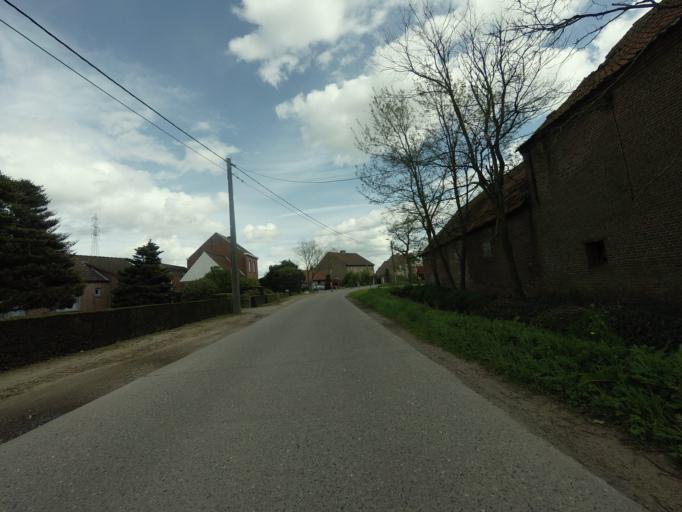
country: BE
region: Flanders
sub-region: Provincie Vlaams-Brabant
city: Kapelle-op-den-Bos
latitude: 51.0272
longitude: 4.4085
